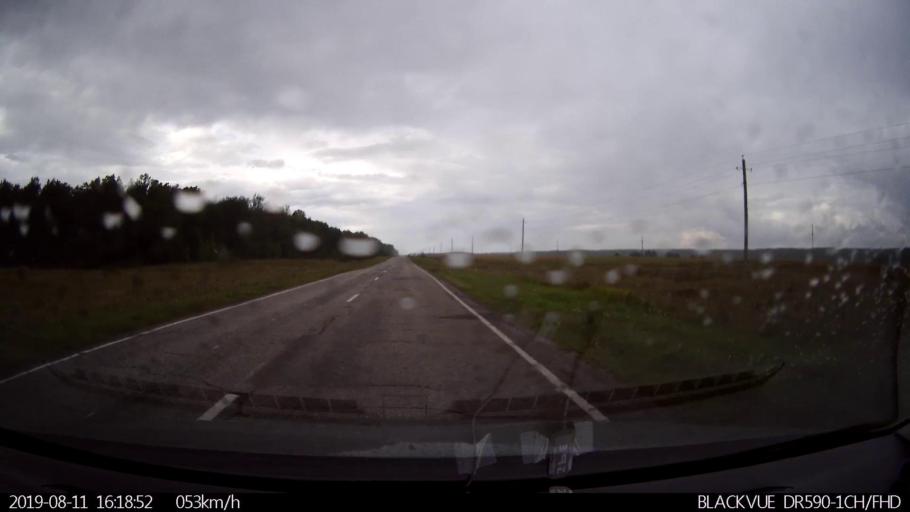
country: RU
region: Ulyanovsk
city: Mayna
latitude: 54.0593
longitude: 47.6093
